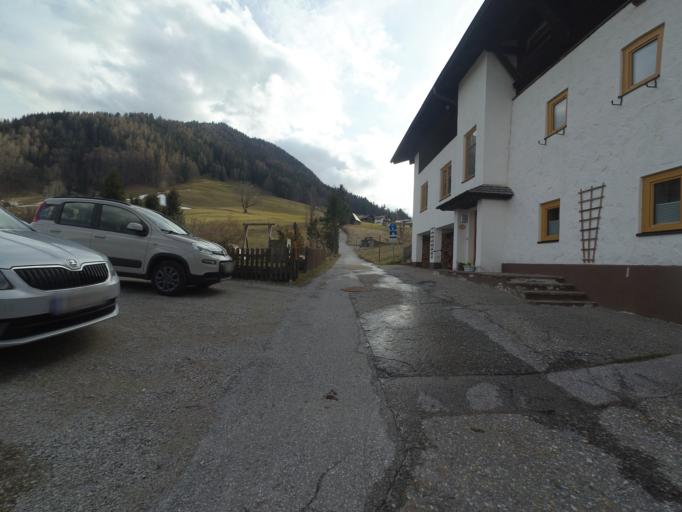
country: AT
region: Salzburg
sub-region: Politischer Bezirk Hallein
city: Hallein
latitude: 47.6586
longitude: 13.0870
